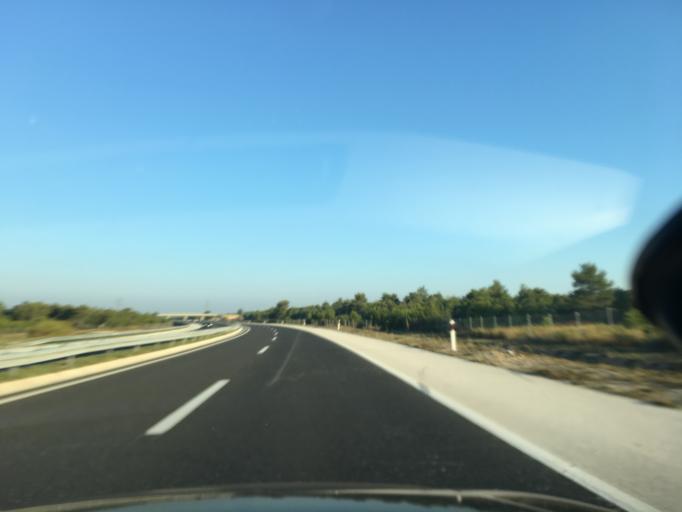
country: HR
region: Sibensko-Kniniska
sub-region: Grad Sibenik
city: Sibenik
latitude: 43.8137
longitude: 15.9132
